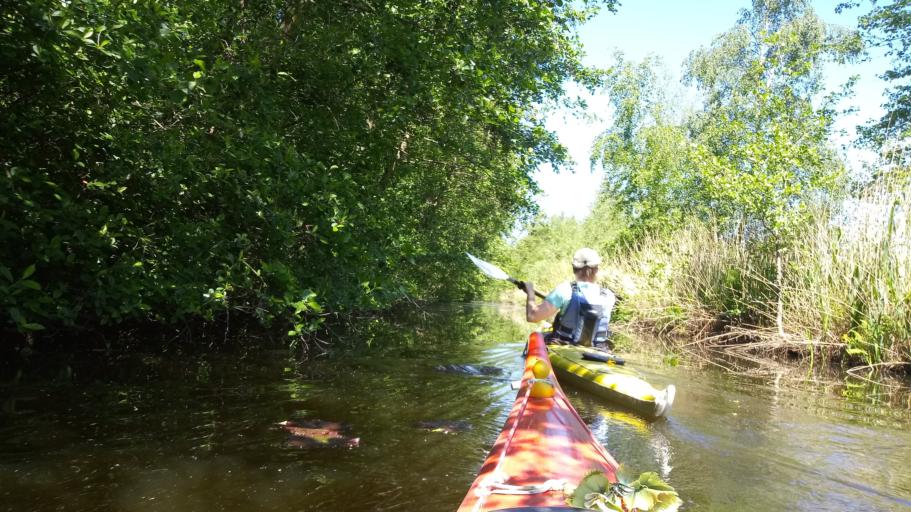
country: NL
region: South Holland
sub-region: Gemeente Nieuwkoop
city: Nieuwkoop
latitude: 52.1598
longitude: 4.8174
